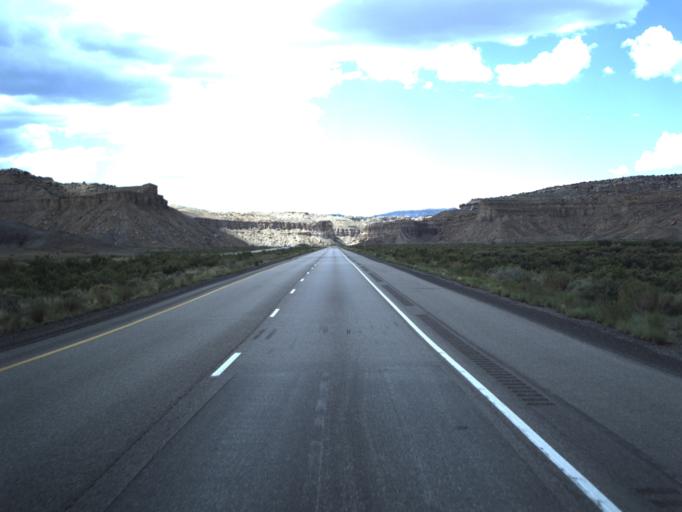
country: US
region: Utah
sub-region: Emery County
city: Ferron
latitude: 38.8100
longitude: -111.2347
